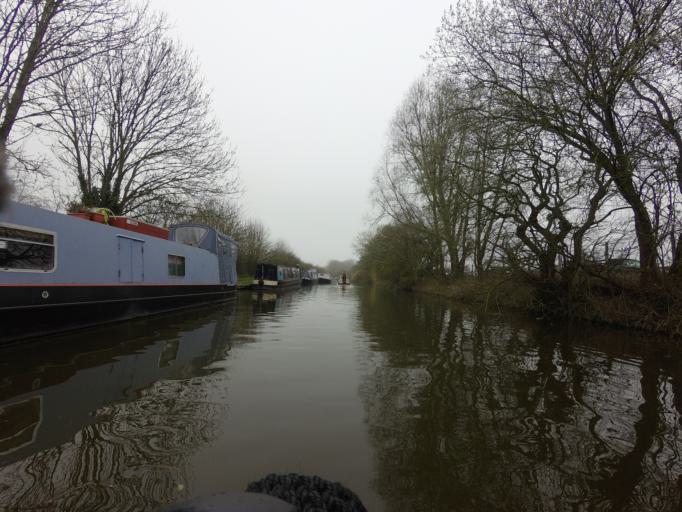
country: GB
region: England
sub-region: Hertfordshire
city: Tring
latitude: 51.7829
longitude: -0.6110
